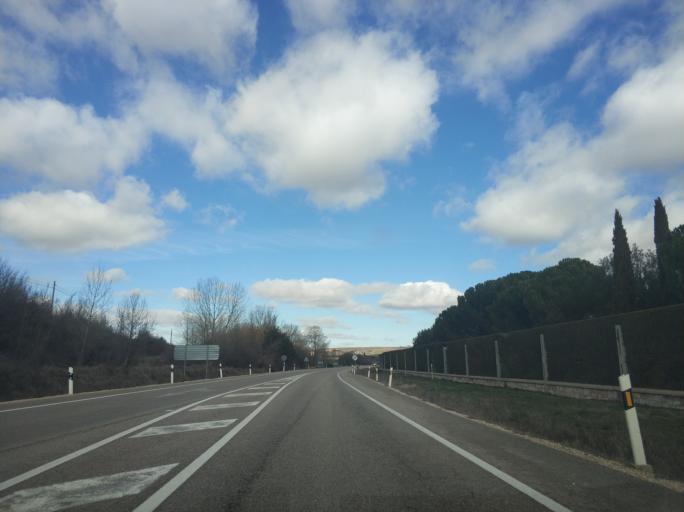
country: ES
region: Castille and Leon
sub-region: Provincia de Burgos
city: Sarracin
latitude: 42.2537
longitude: -3.6891
